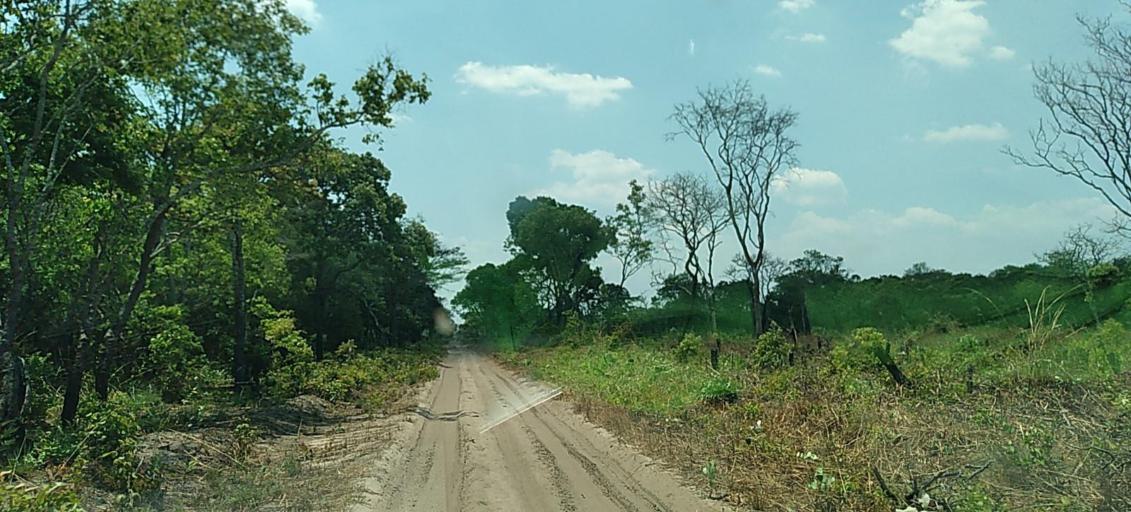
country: CD
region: Katanga
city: Kolwezi
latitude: -11.3120
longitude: 25.2358
